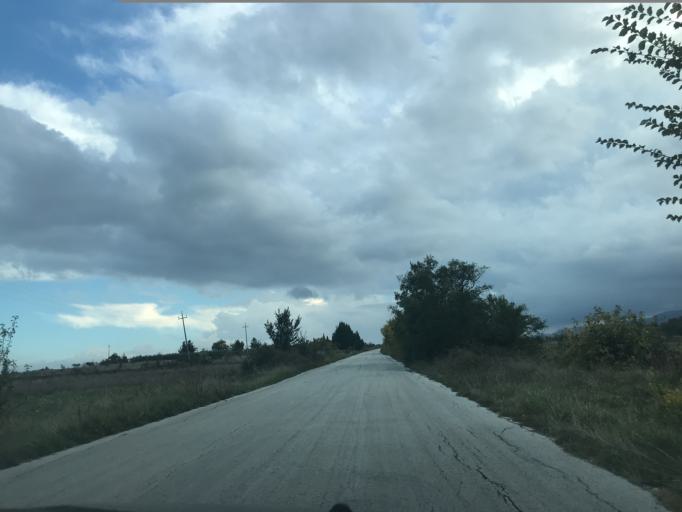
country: IT
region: Molise
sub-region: Provincia di Isernia
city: Bagnoli del Trigno
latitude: 41.6929
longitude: 14.4621
